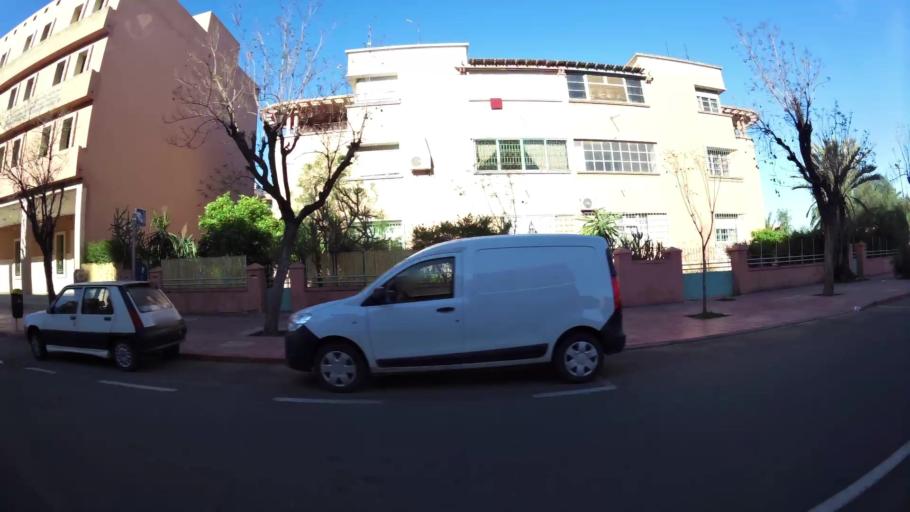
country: MA
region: Marrakech-Tensift-Al Haouz
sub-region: Marrakech
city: Marrakesh
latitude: 31.6331
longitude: -8.0168
